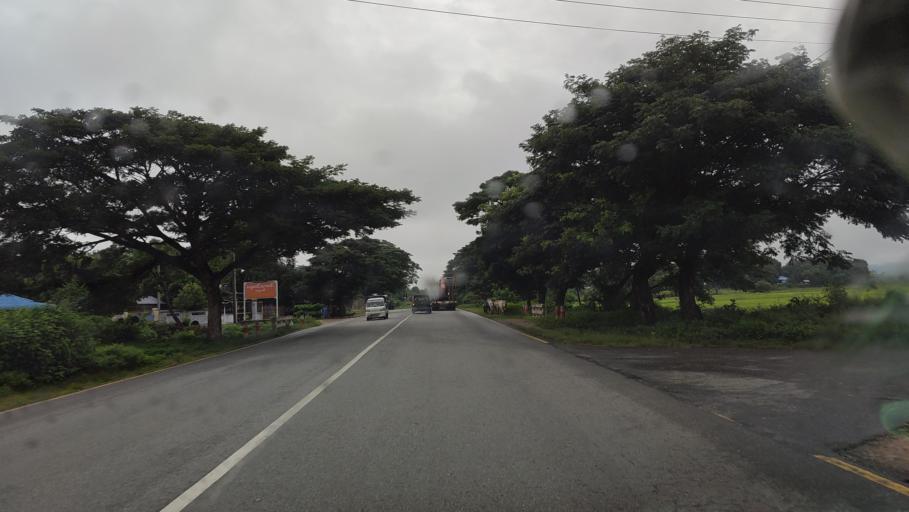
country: MM
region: Mandalay
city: Pyinmana
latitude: 19.9655
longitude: 96.2529
